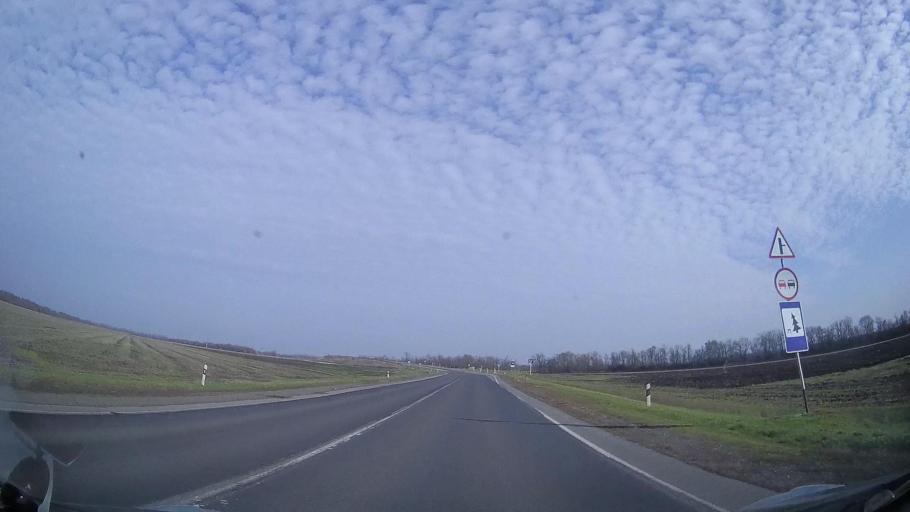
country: RU
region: Rostov
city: Tselina
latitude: 46.5238
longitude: 41.1632
